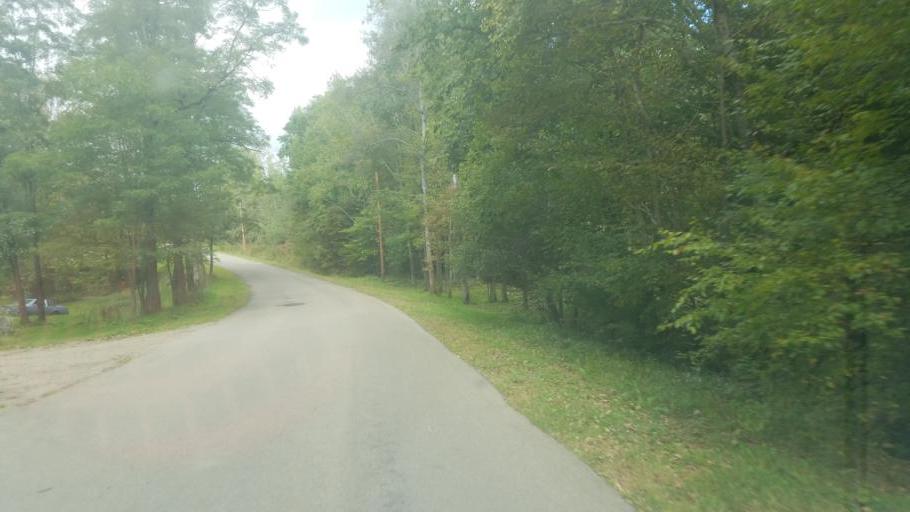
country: US
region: New York
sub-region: Cattaraugus County
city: Weston Mills
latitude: 42.1500
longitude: -78.3574
